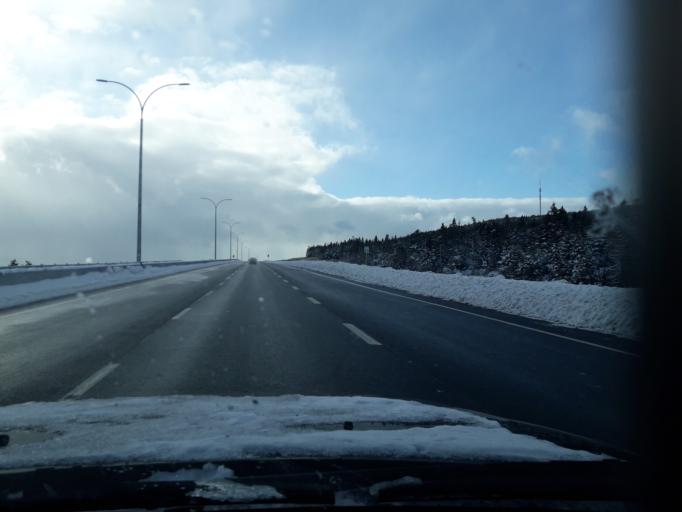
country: CA
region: Newfoundland and Labrador
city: Mount Pearl
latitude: 47.5385
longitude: -52.7733
